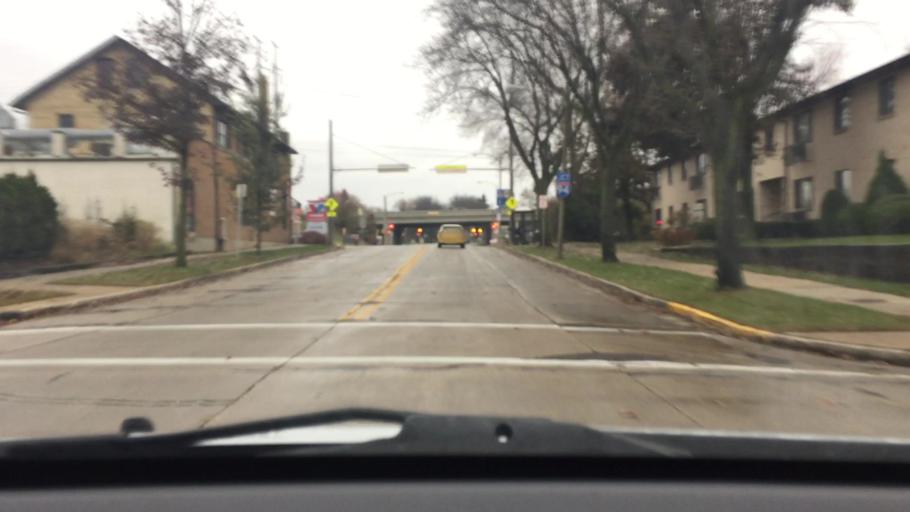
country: US
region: Wisconsin
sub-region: Milwaukee County
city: West Allis
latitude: 43.0320
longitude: -87.9974
